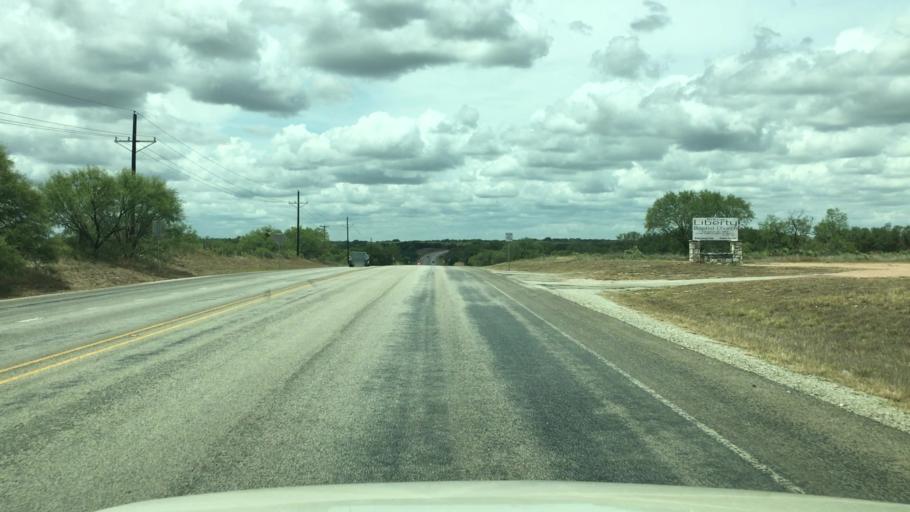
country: US
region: Texas
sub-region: McCulloch County
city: Brady
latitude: 31.0032
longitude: -99.1886
